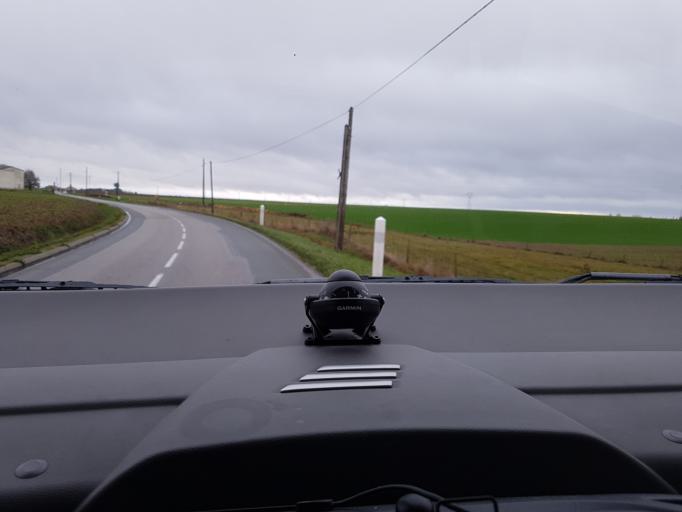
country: FR
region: Haute-Normandie
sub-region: Departement de l'Eure
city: Pont-Saint-Pierre
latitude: 49.3040
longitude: 1.3196
